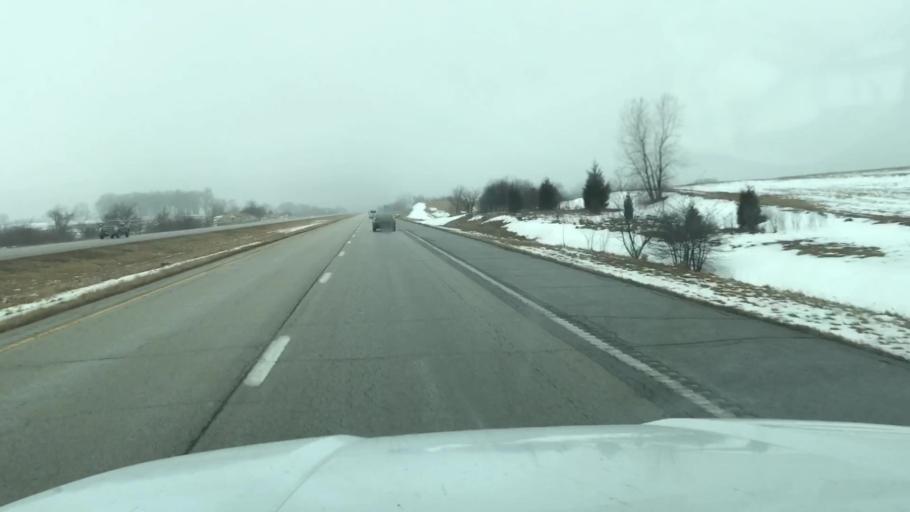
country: US
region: Missouri
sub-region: Andrew County
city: Country Club Village
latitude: 39.7480
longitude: -94.6896
